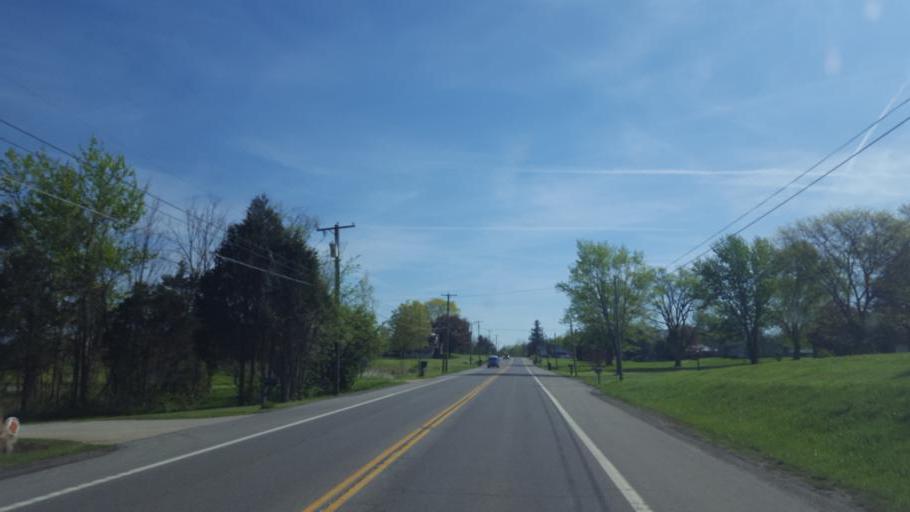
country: US
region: Ohio
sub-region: Ashland County
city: Ashland
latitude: 40.8312
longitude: -82.3760
